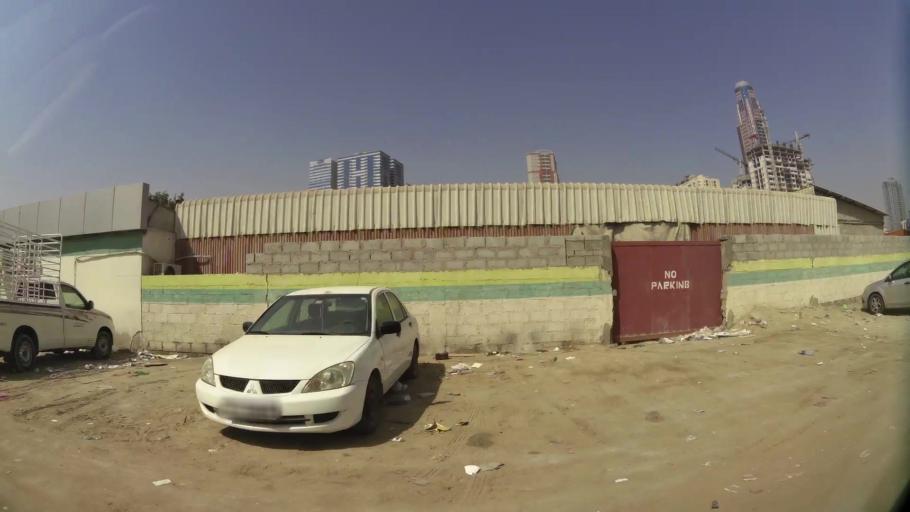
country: AE
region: Ash Shariqah
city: Sharjah
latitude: 25.3061
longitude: 55.3869
